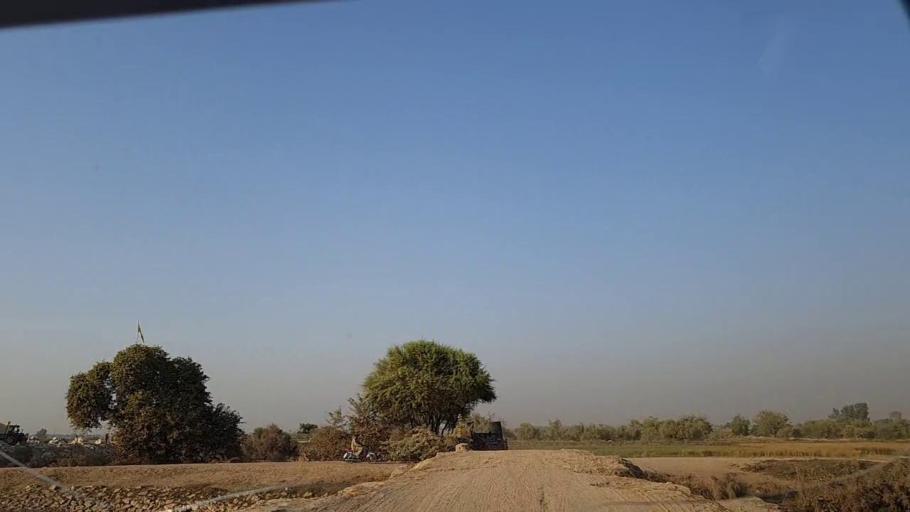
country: PK
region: Sindh
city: Rustam jo Goth
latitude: 27.9738
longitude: 68.8053
